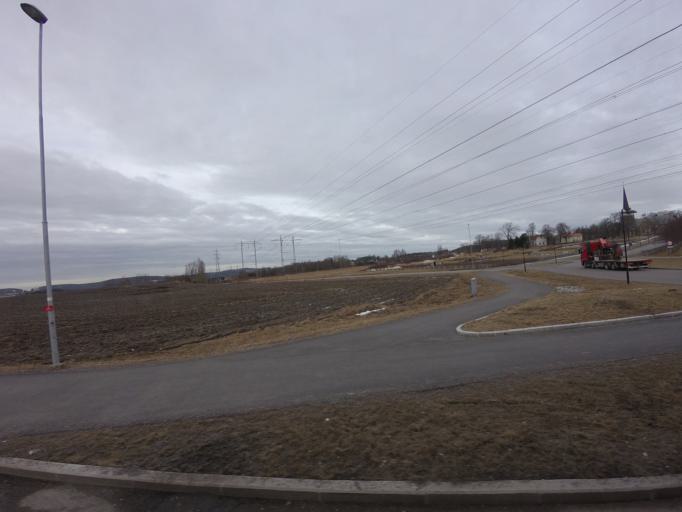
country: NO
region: Akershus
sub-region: Skedsmo
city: Lillestrom
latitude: 59.9910
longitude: 11.0486
